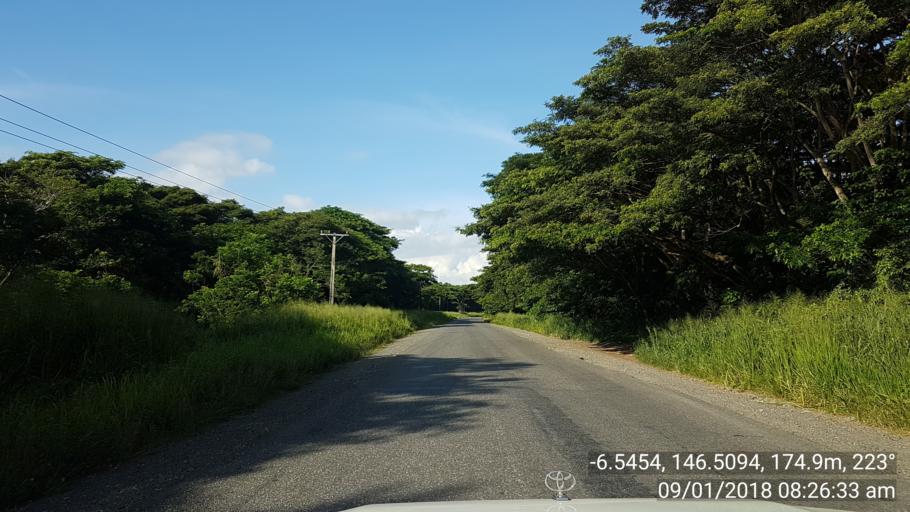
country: PG
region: Morobe
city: Lae
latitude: -6.5453
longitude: 146.5098
